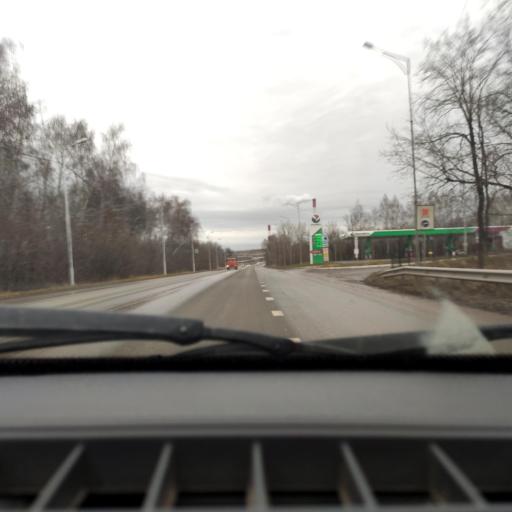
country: RU
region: Bashkortostan
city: Blagoveshchensk
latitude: 54.9045
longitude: 56.0544
